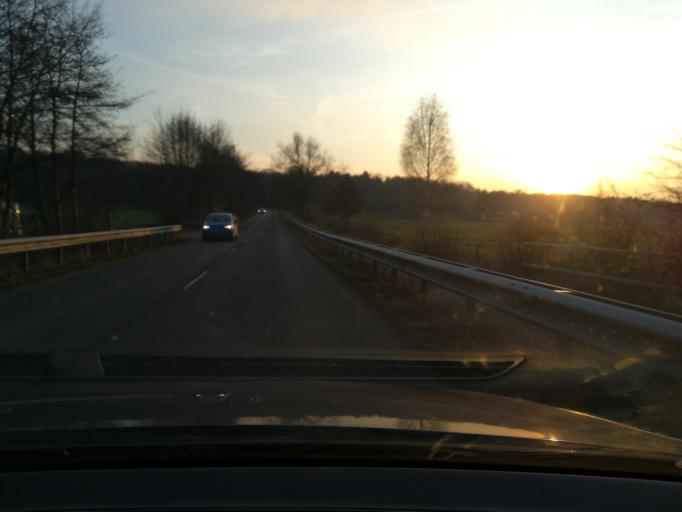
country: DE
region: Schleswig-Holstein
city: Escheburg
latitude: 53.4550
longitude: 10.3155
